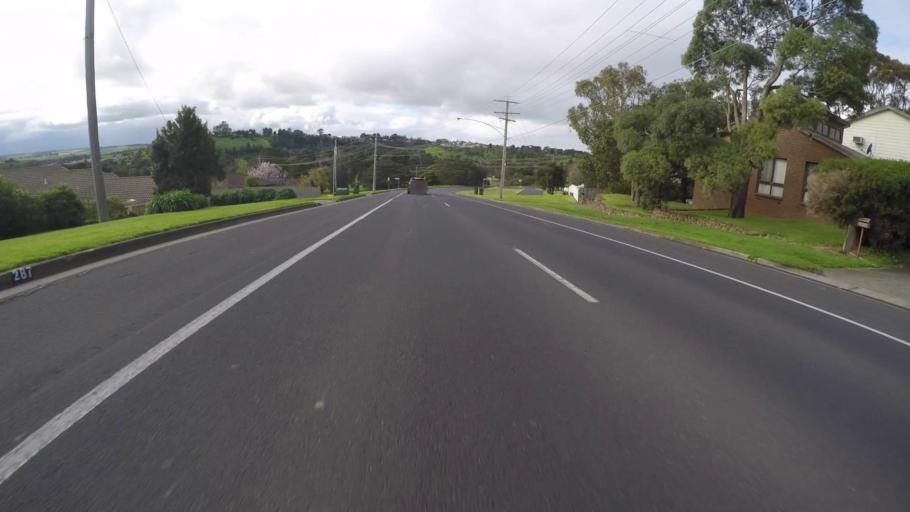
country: AU
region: Victoria
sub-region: Greater Geelong
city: Wandana Heights
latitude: -38.1503
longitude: 144.3142
